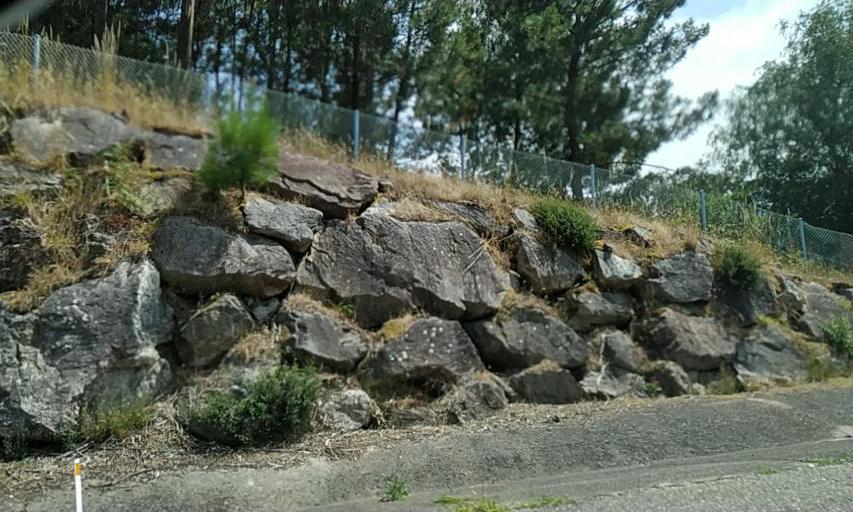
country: ES
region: Galicia
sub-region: Provincia de Pontevedra
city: Baiona
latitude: 42.1012
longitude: -8.8203
